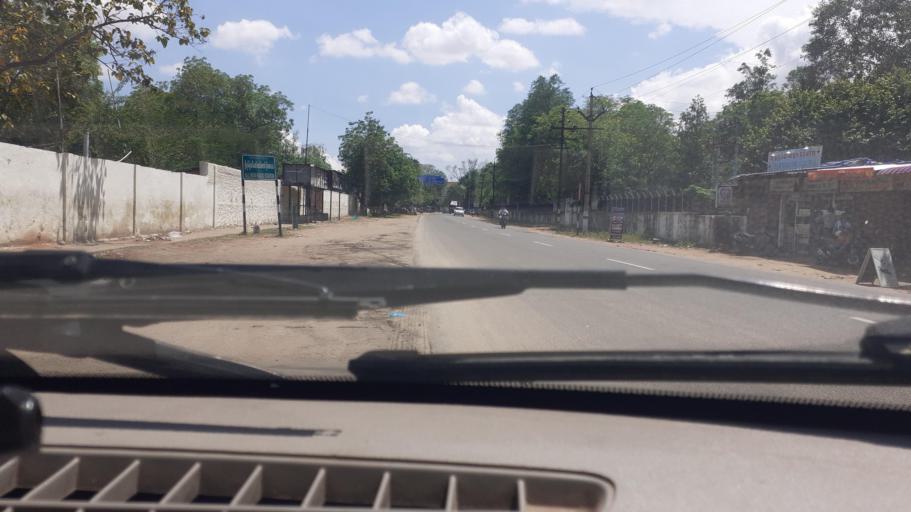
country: IN
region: Tamil Nadu
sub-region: Tirunelveli Kattabo
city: Tirunelveli
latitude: 8.7187
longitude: 77.7343
